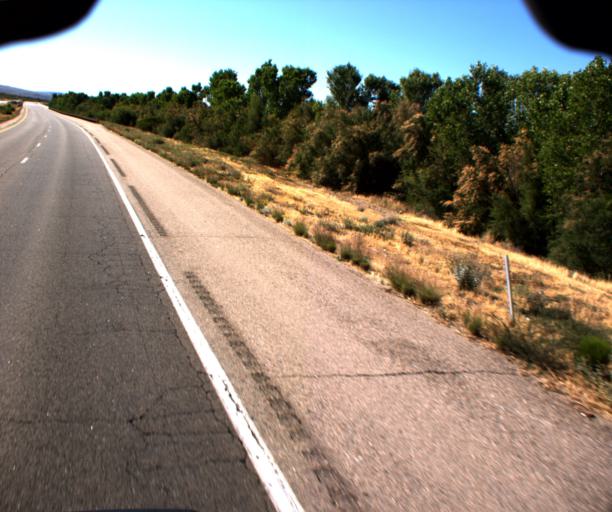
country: US
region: Arizona
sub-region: Yavapai County
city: Bagdad
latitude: 34.6668
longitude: -113.5854
